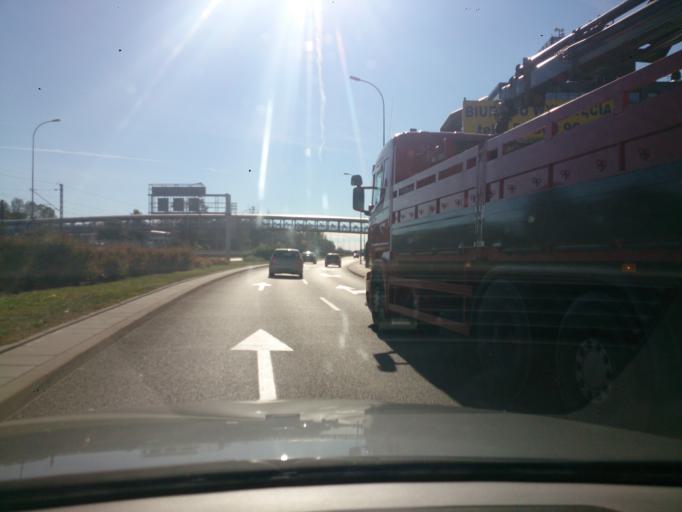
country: PL
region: Pomeranian Voivodeship
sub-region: Gdynia
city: Gdynia
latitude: 54.4987
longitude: 18.5340
